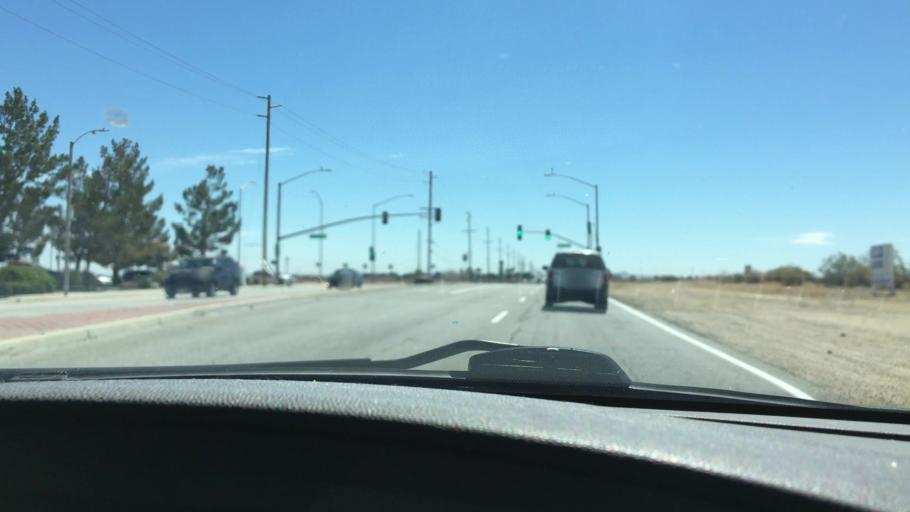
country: US
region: California
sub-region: Los Angeles County
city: Lancaster
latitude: 34.6459
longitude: -118.1379
